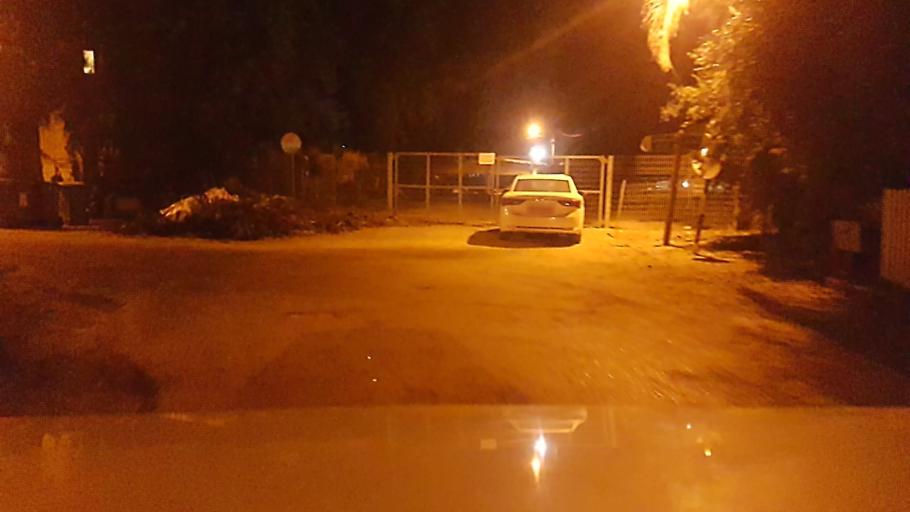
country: IL
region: Central District
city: Nehalim
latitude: 32.0766
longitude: 34.9272
